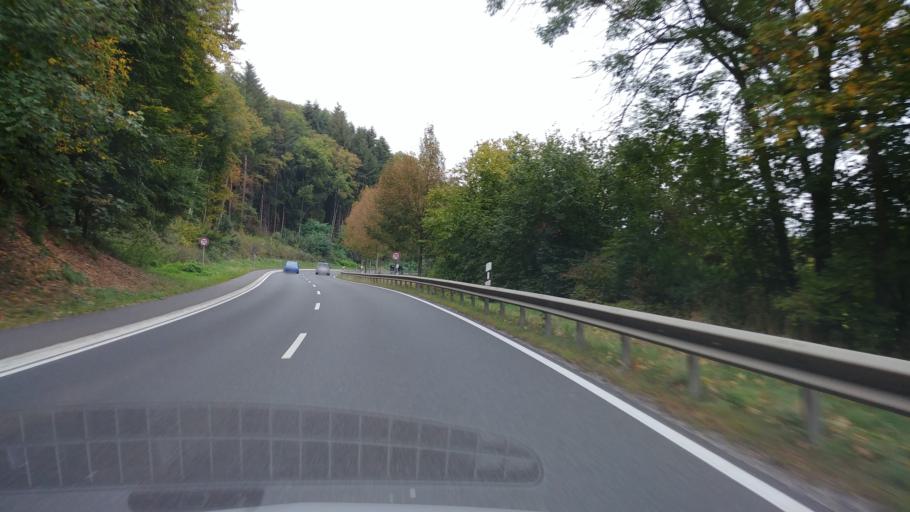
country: DE
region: Rheinland-Pfalz
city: Holzheim
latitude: 50.3568
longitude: 8.0349
